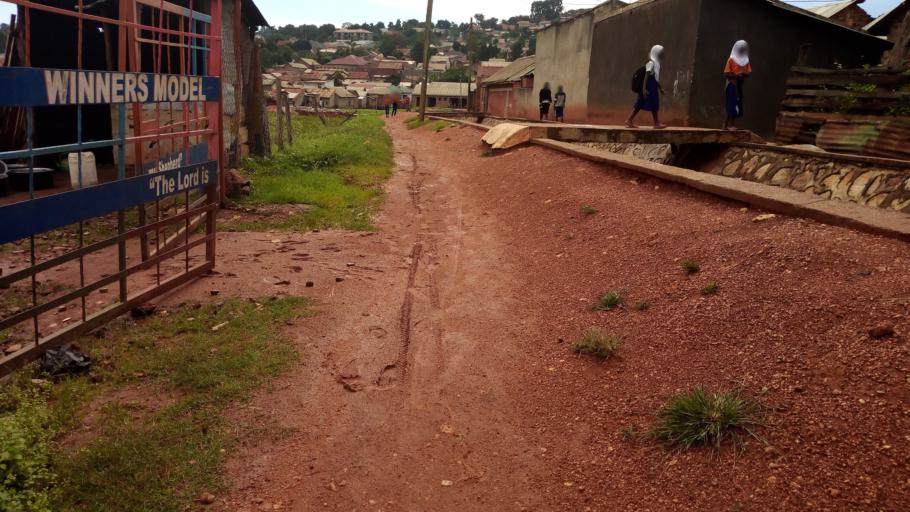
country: UG
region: Central Region
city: Kampala Central Division
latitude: 0.3756
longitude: 32.5553
